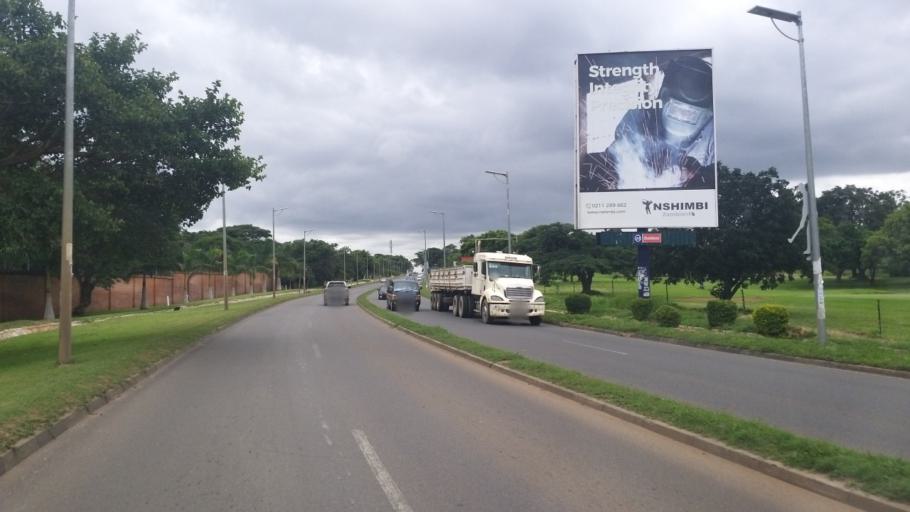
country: ZM
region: Lusaka
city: Lusaka
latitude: -15.4241
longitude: 28.3278
